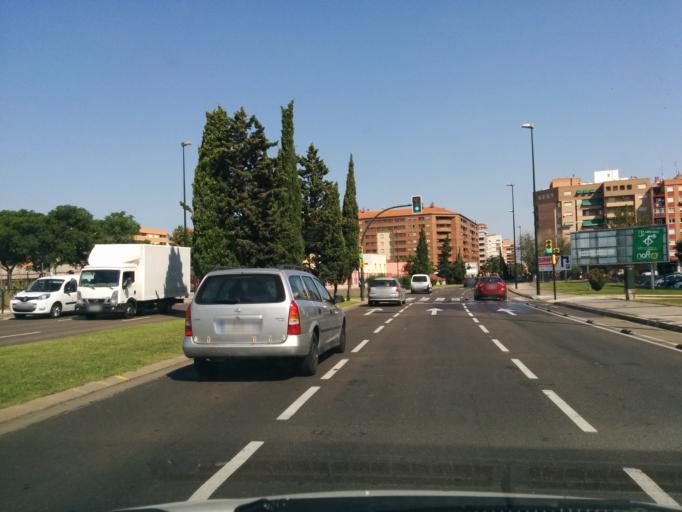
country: ES
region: Aragon
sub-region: Provincia de Zaragoza
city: Zaragoza
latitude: 41.6591
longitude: -0.8625
